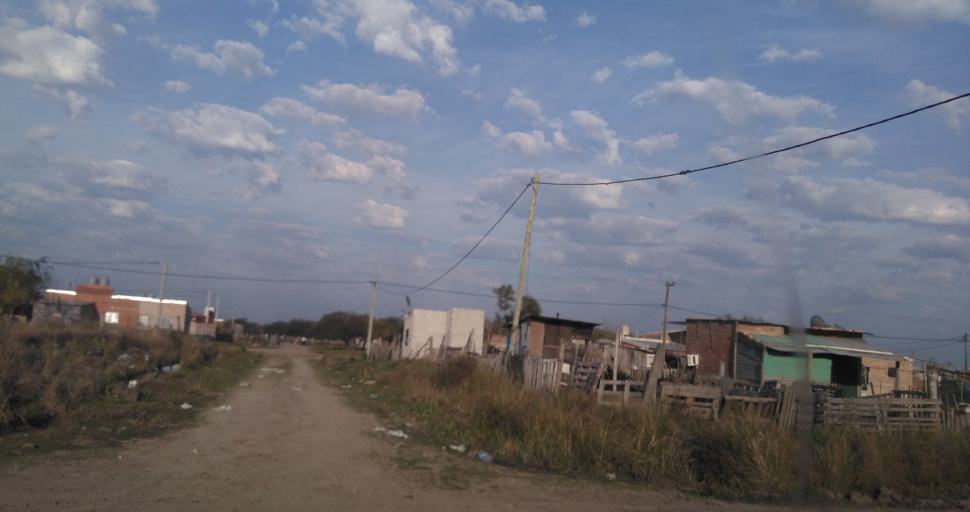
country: AR
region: Chaco
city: Fontana
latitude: -27.4589
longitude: -59.0451
